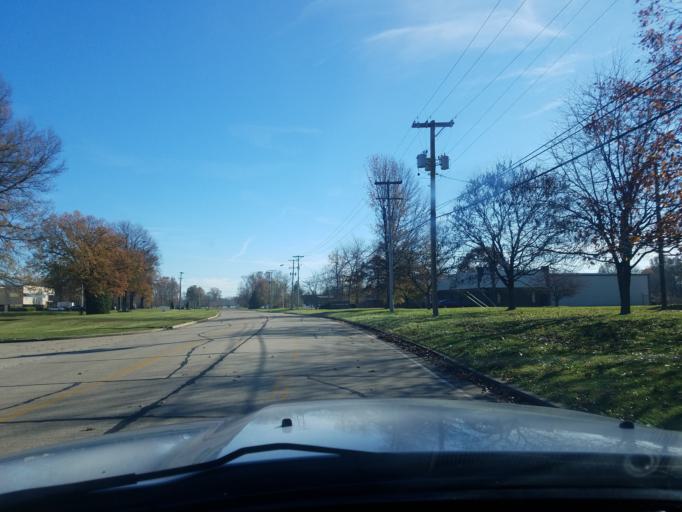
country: US
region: Kentucky
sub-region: Jefferson County
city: Pleasure Ridge Park
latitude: 38.1509
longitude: -85.8948
